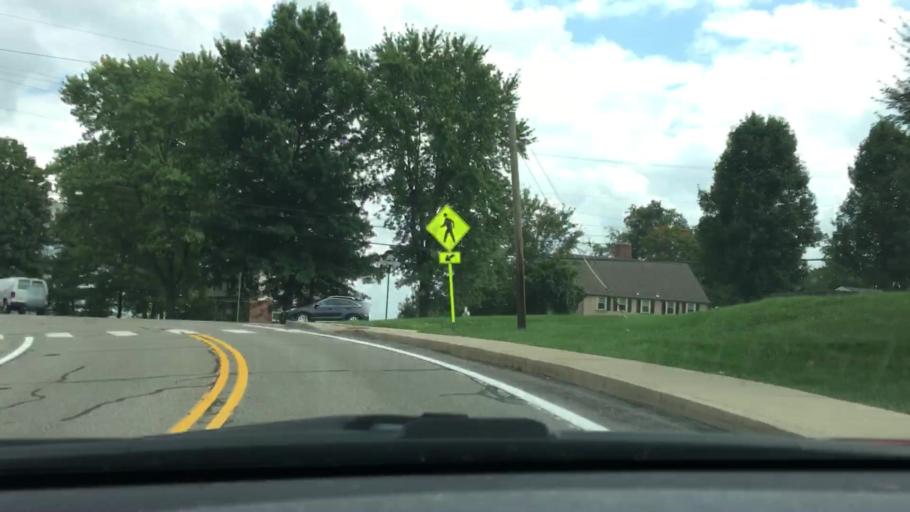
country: US
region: Pennsylvania
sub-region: Allegheny County
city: Mount Lebanon
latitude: 40.3500
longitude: -80.0615
